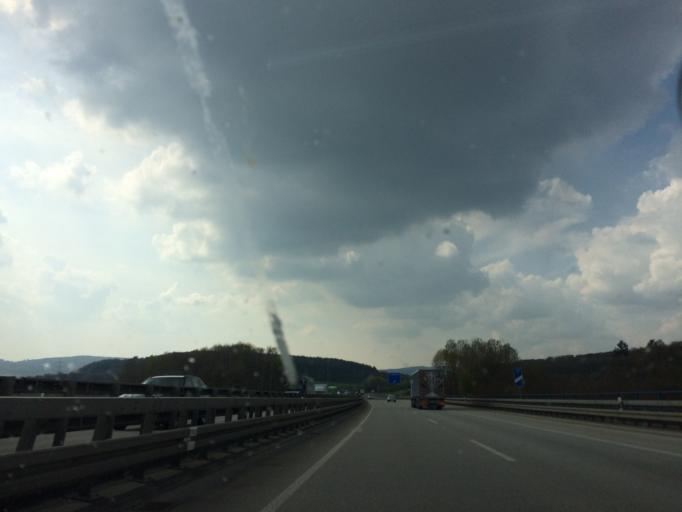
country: DE
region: Hesse
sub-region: Regierungsbezirk Giessen
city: Ehringshausen
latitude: 50.6188
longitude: 8.3909
